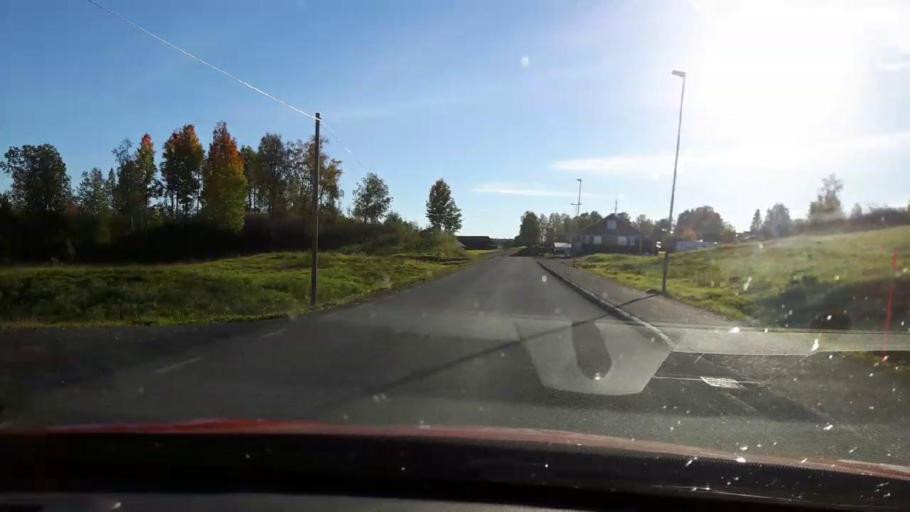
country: SE
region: Jaemtland
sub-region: OEstersunds Kommun
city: Lit
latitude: 63.8157
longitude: 14.8101
